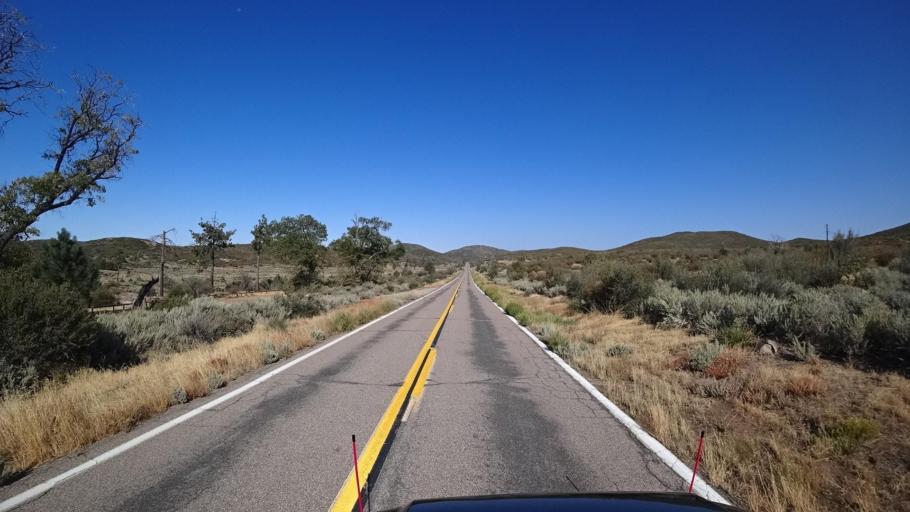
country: US
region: California
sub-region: San Diego County
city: Pine Valley
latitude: 32.9147
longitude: -116.4662
